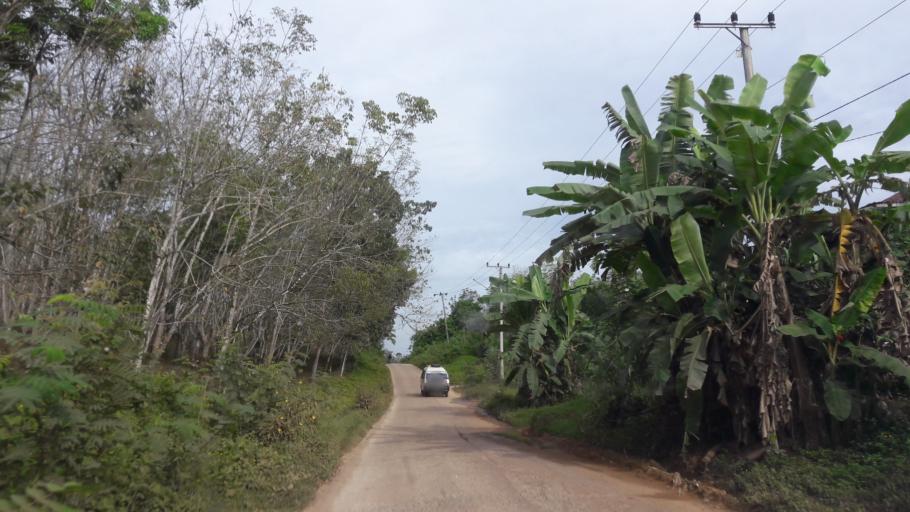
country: ID
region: South Sumatra
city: Gunungmegang Dalam
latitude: -3.2870
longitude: 103.7192
